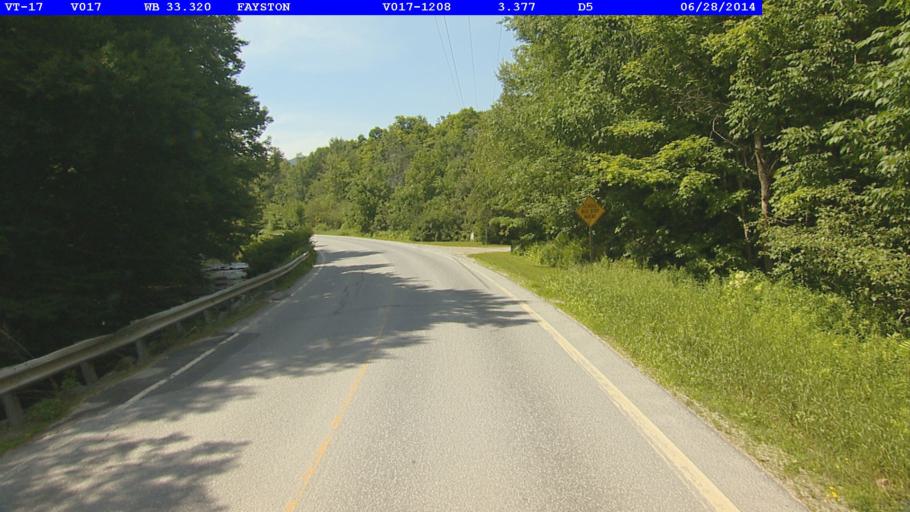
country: US
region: Vermont
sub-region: Washington County
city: Waterbury
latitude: 44.1922
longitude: -72.8855
